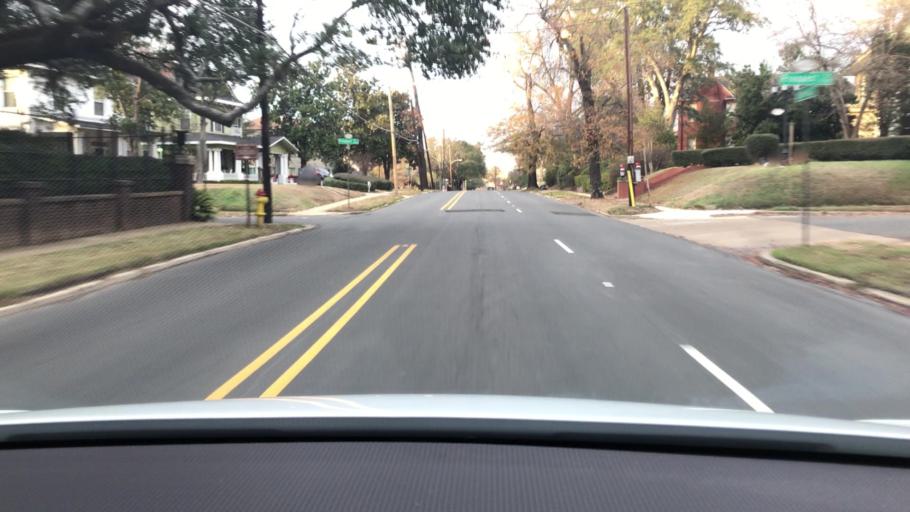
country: US
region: Louisiana
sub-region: Bossier Parish
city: Bossier City
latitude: 32.4876
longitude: -93.7499
